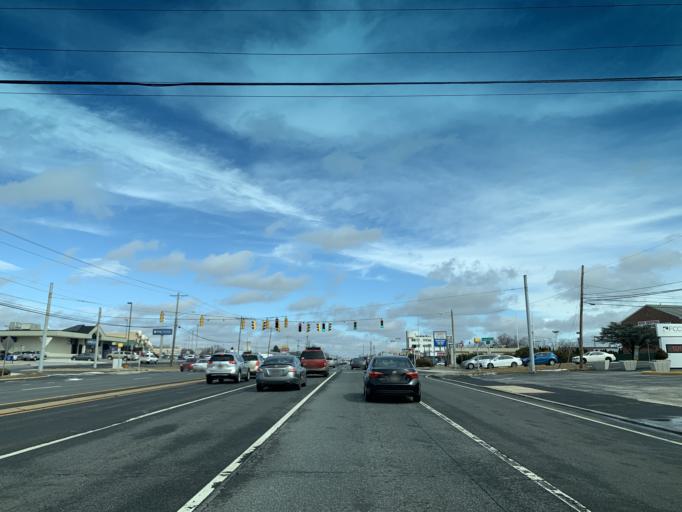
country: US
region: Delaware
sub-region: New Castle County
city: Pike Creek Valley
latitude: 39.7209
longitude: -75.6636
